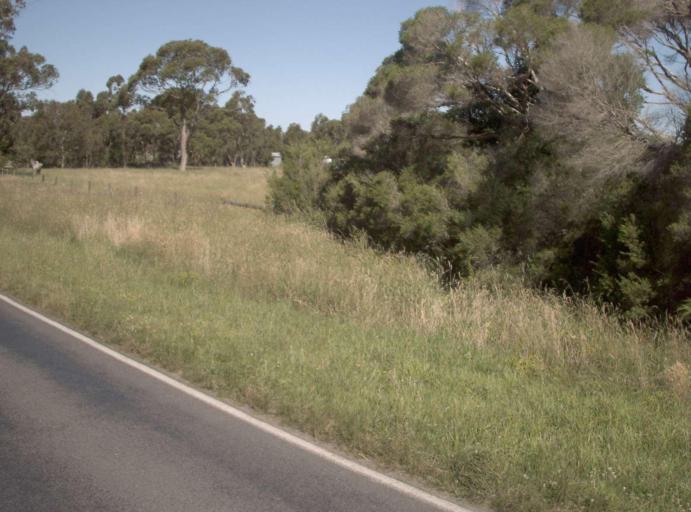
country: AU
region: Victoria
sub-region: Latrobe
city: Morwell
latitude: -38.6416
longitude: 146.4865
